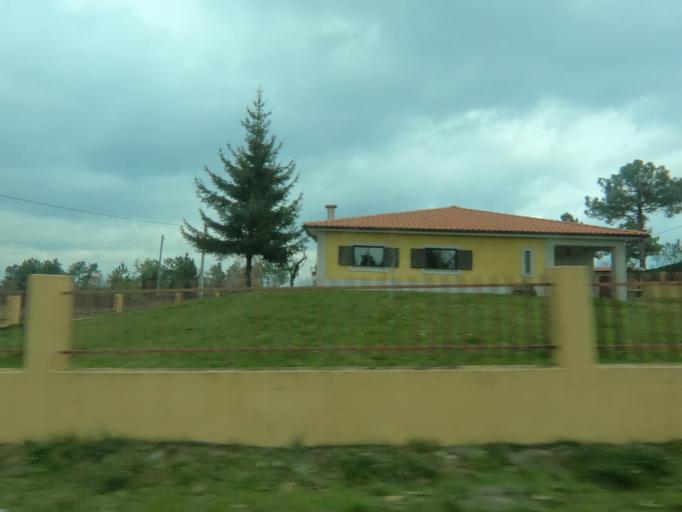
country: PT
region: Vila Real
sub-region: Sabrosa
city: Sabrosa
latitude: 41.3323
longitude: -7.6455
